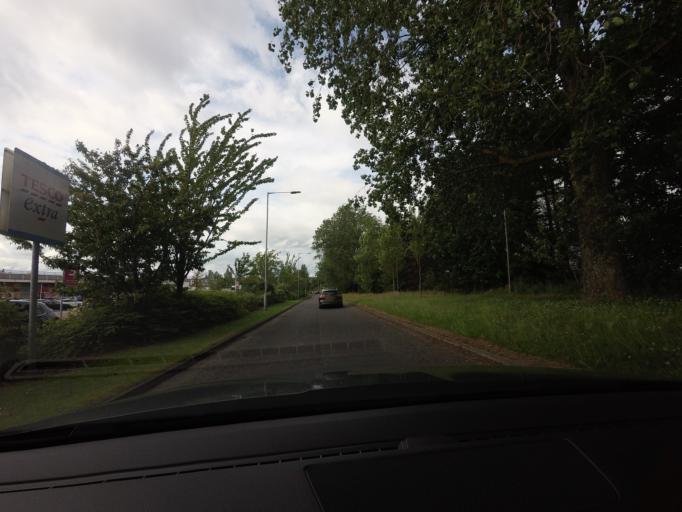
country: GB
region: Scotland
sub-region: Highland
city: Inverness
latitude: 57.4698
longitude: -4.1877
